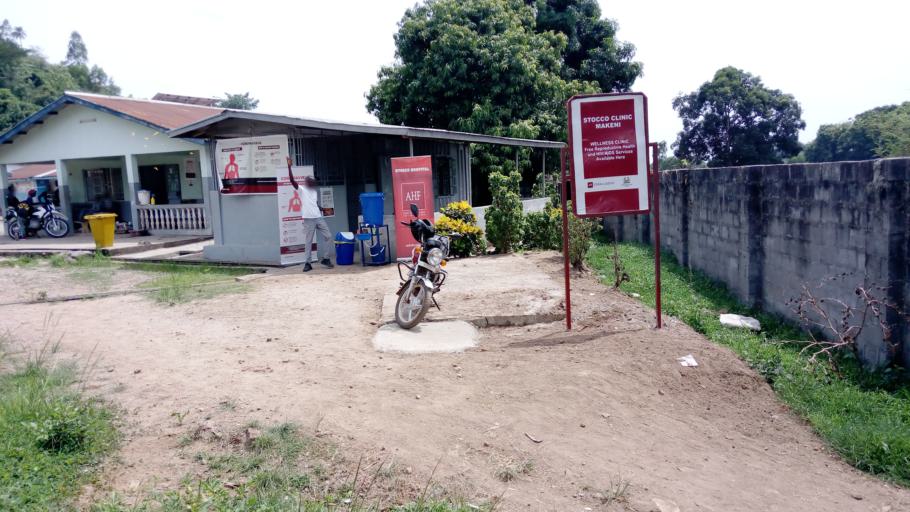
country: SL
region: Northern Province
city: Makeni
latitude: 8.8906
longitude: -12.0619
